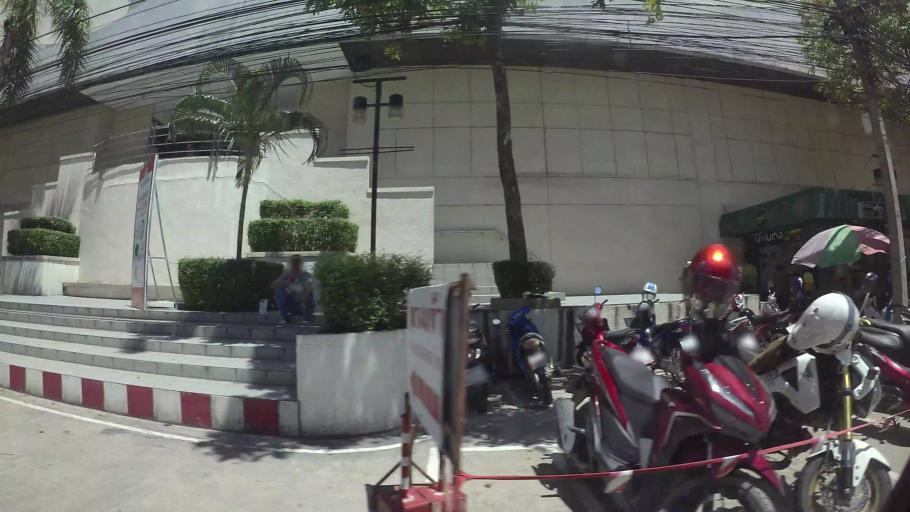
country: TH
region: Chon Buri
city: Si Racha
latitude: 13.1688
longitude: 100.9308
